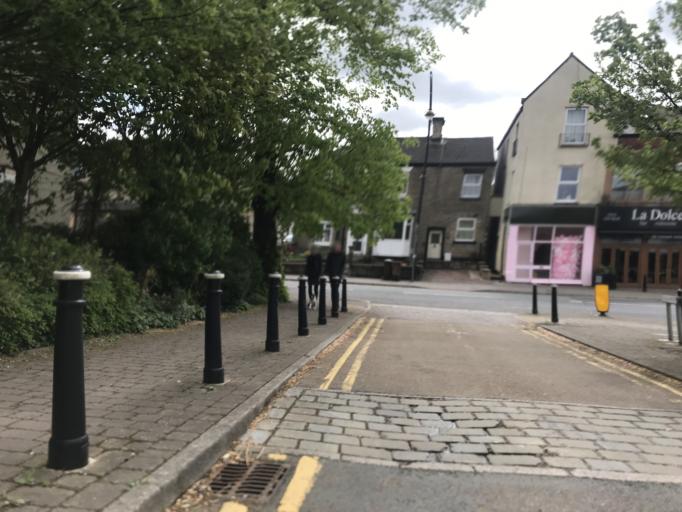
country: GB
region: England
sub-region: Borough of Stockport
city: Marple
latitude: 53.3948
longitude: -2.0622
